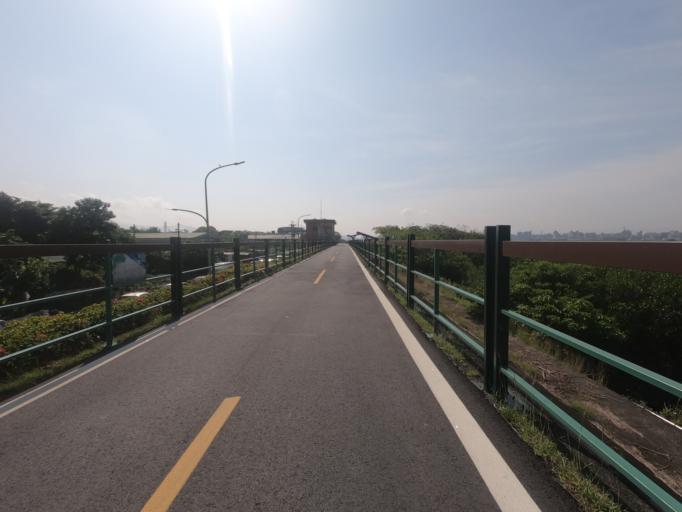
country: TW
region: Taipei
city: Taipei
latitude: 25.1074
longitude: 121.4698
